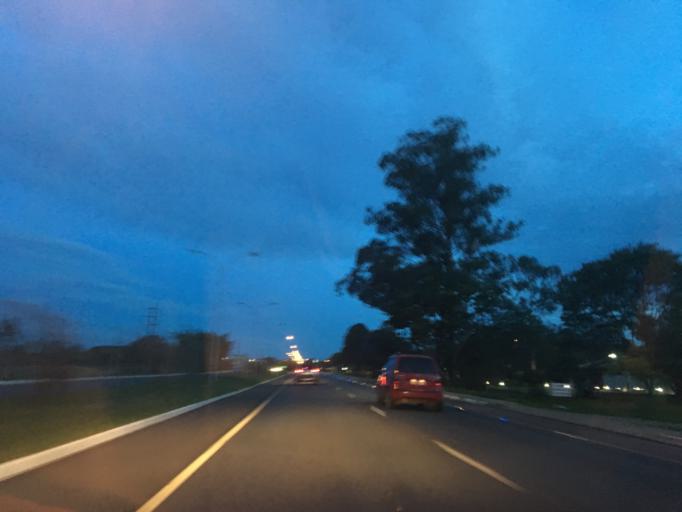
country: BR
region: Federal District
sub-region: Brasilia
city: Brasilia
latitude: -15.8527
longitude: -47.8452
